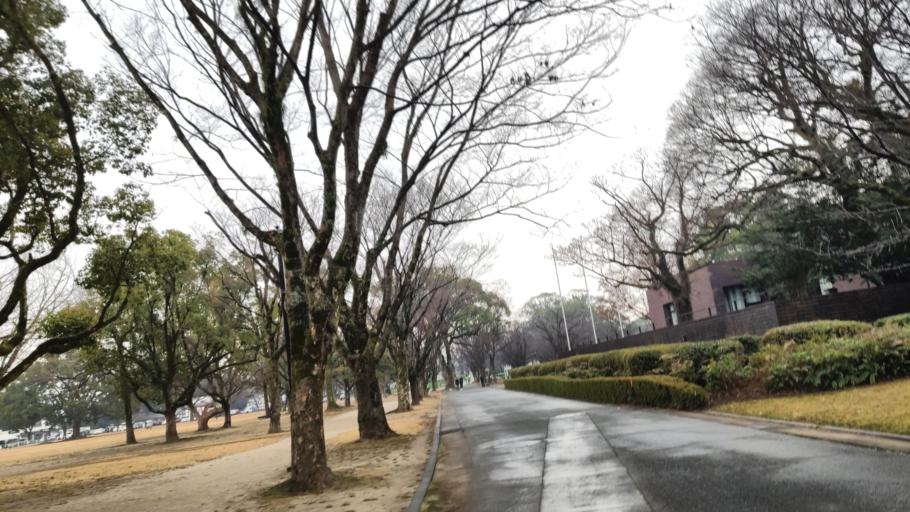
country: JP
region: Kumamoto
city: Kumamoto
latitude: 32.8076
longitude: 130.7011
